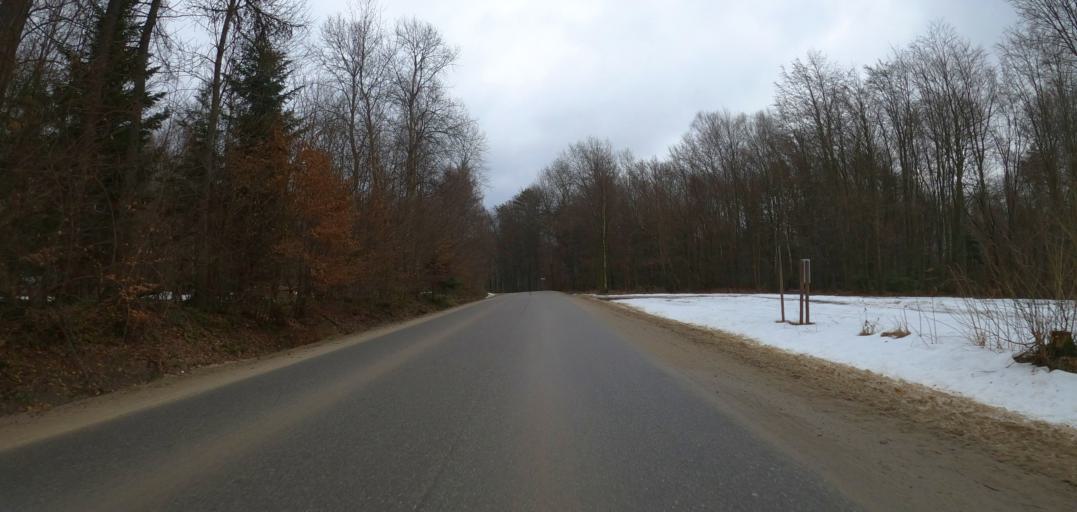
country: PL
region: Subcarpathian Voivodeship
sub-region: Powiat debicki
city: Debica
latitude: 49.9843
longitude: 21.4119
